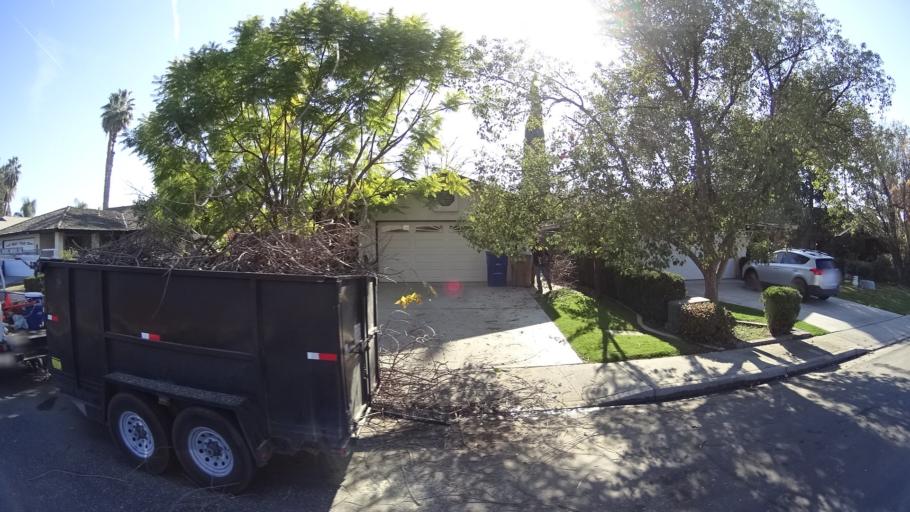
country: US
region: California
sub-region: Kern County
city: Greenacres
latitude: 35.3212
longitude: -119.1210
